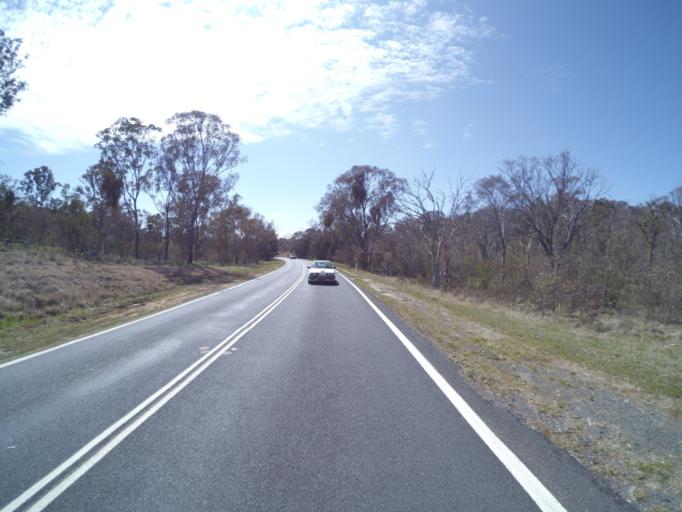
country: AU
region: Australian Capital Territory
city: Macarthur
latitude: -35.4533
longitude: 149.0441
